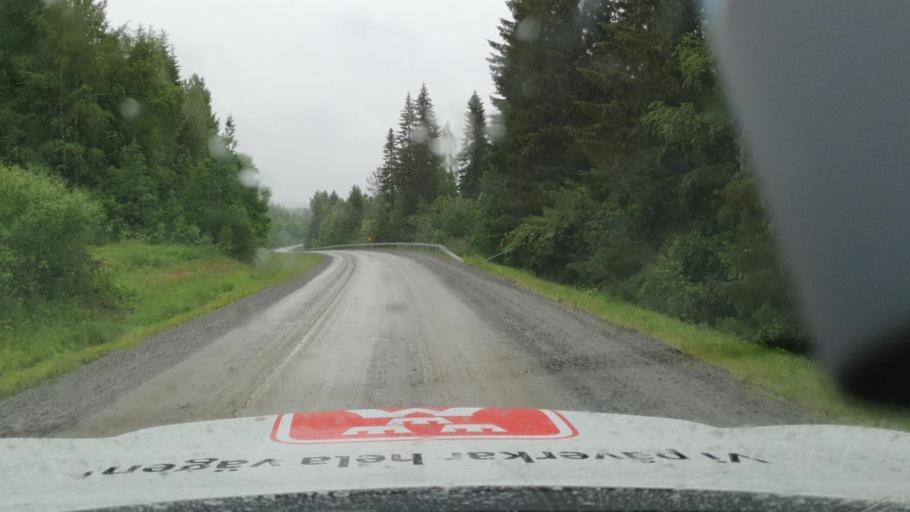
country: SE
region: Vaesterbotten
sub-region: Bjurholms Kommun
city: Bjurholm
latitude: 63.9049
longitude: 19.3977
